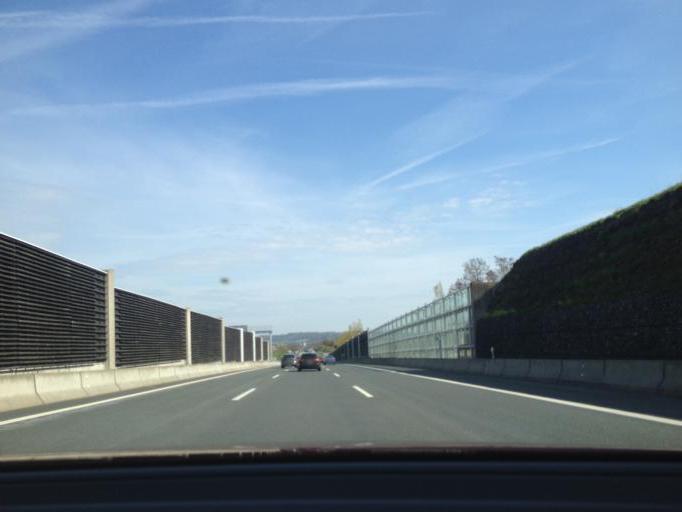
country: DE
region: Bavaria
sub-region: Upper Franconia
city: Bayreuth
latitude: 49.9397
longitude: 11.6051
